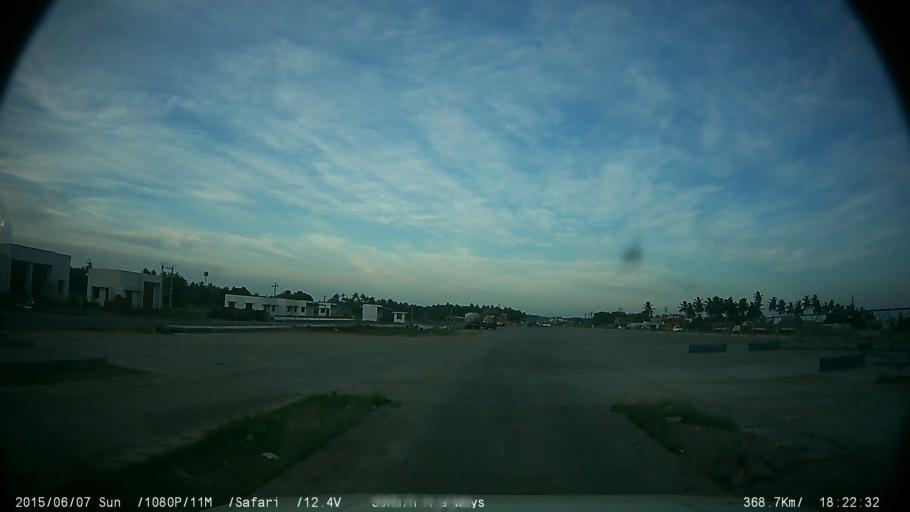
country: IN
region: Tamil Nadu
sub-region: Coimbatore
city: Sulur
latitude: 11.0952
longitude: 77.1511
